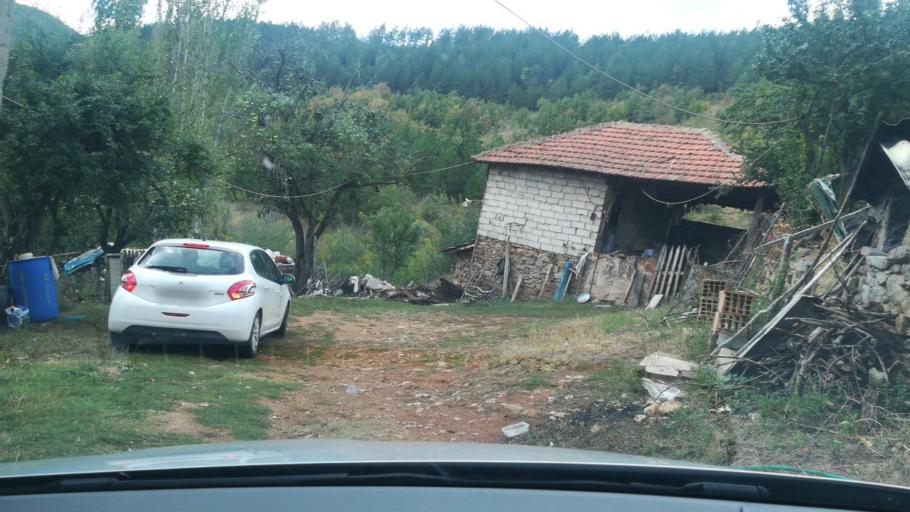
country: MK
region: Makedonska Kamenica
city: Makedonska Kamenica
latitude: 42.0029
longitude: 22.6067
